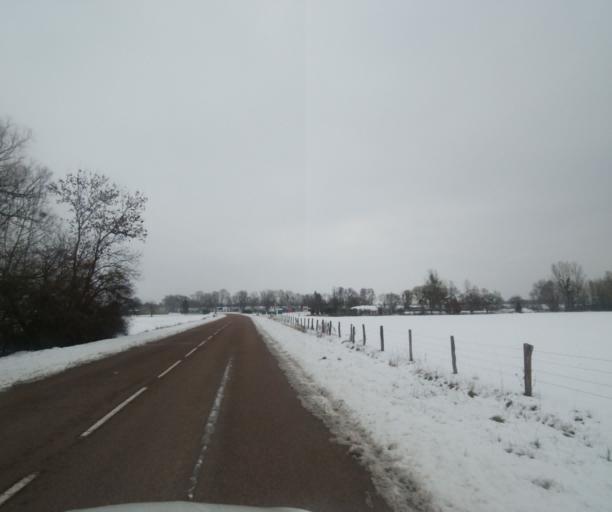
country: FR
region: Champagne-Ardenne
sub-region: Departement de la Haute-Marne
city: Villiers-en-Lieu
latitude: 48.5932
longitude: 4.8505
